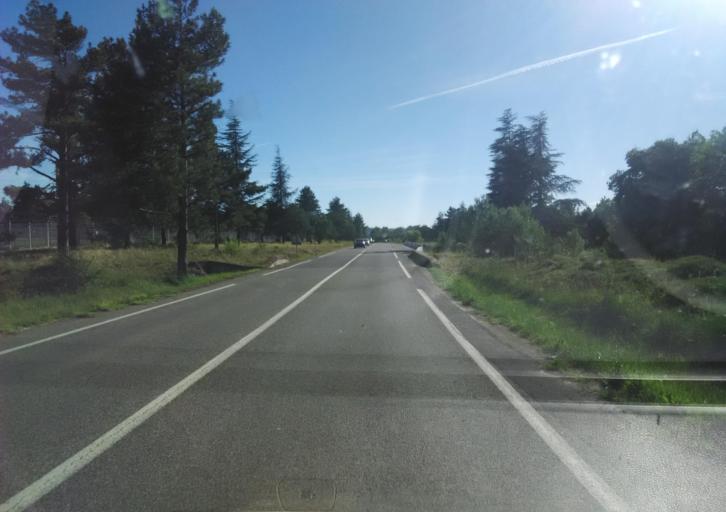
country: FR
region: Provence-Alpes-Cote d'Azur
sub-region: Departement du Var
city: Vinon-sur-Verdon
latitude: 43.7075
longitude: 5.7604
